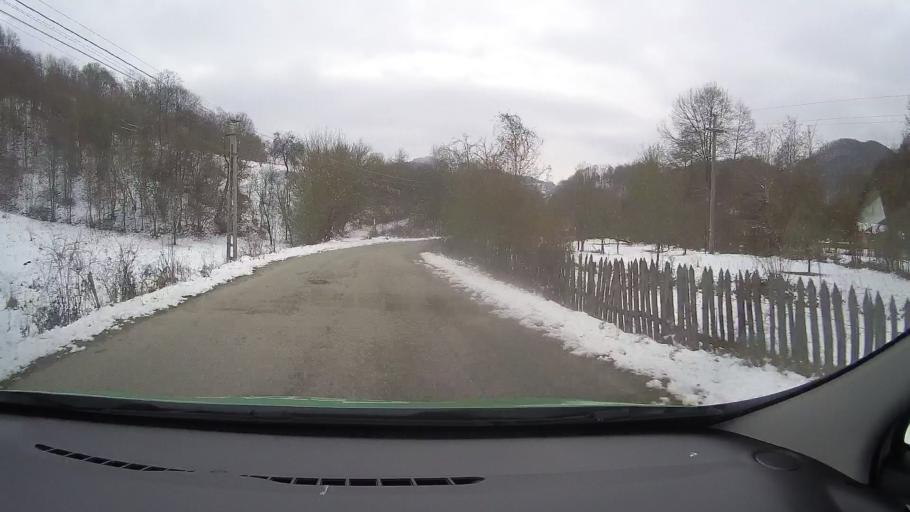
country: RO
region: Hunedoara
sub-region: Comuna Balsa
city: Balsa
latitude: 46.0491
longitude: 23.0706
